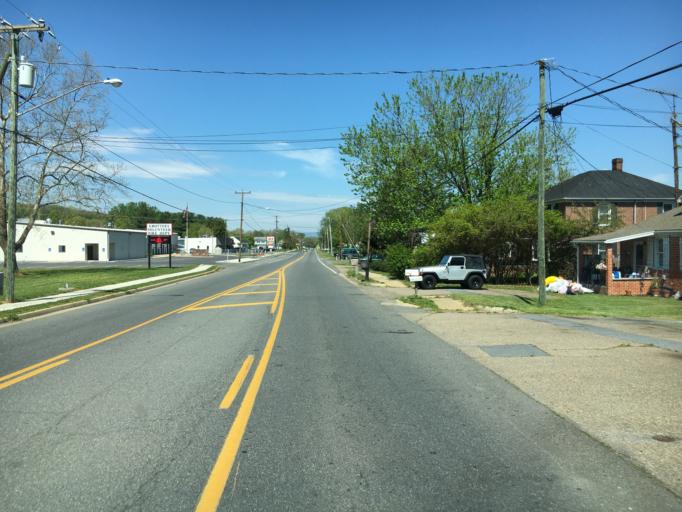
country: US
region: Virginia
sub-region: Rockingham County
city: Grottoes
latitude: 38.2615
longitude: -78.8232
